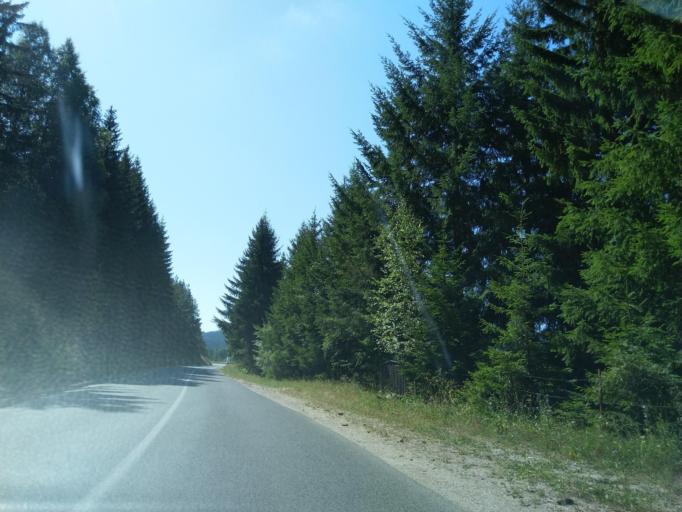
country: RS
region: Central Serbia
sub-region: Zlatiborski Okrug
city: Nova Varos
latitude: 43.4360
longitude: 19.8238
